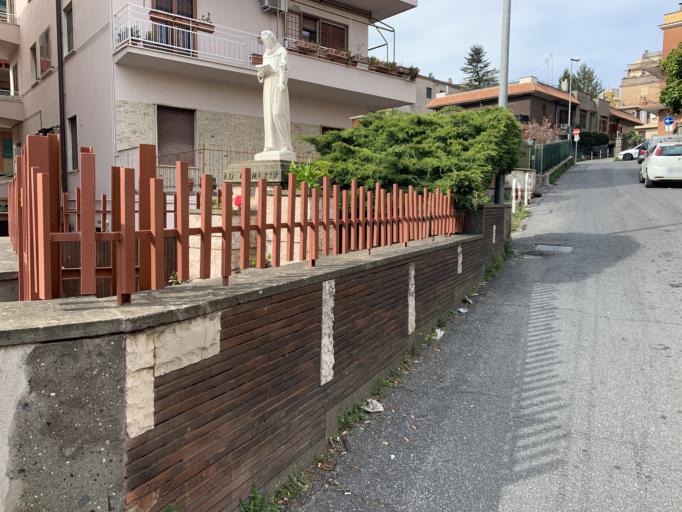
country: IT
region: Latium
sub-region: Citta metropolitana di Roma Capitale
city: Grottaferrata
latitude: 41.7690
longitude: 12.6661
